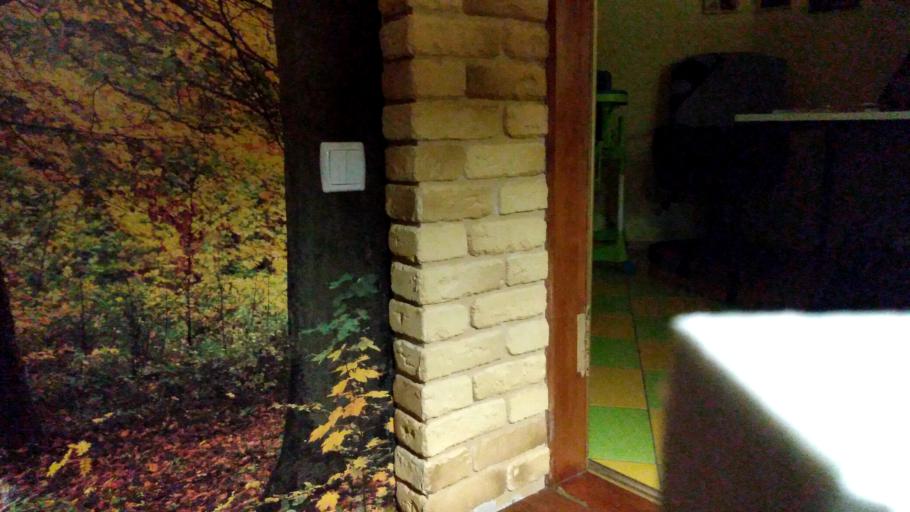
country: RU
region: Vologda
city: Lipin Bor
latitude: 61.0895
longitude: 37.9285
